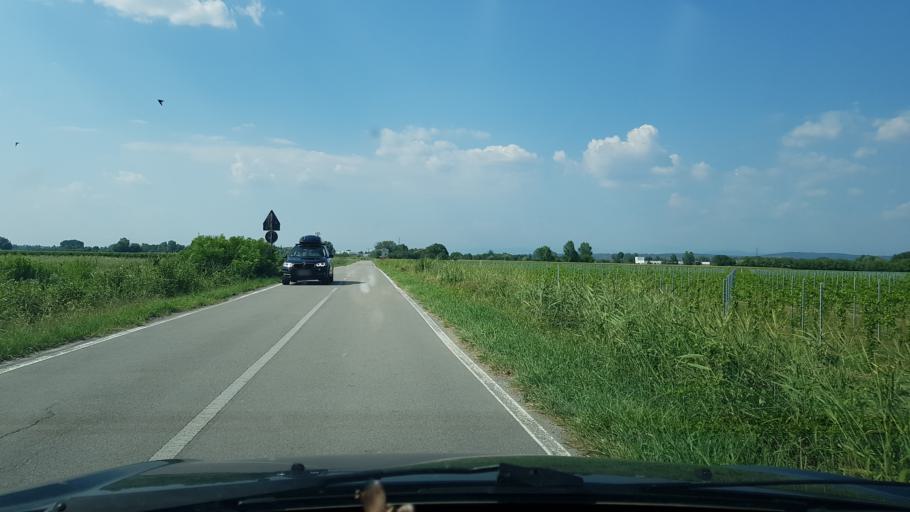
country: IT
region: Friuli Venezia Giulia
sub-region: Provincia di Gorizia
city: Staranzano
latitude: 45.7804
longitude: 13.5105
